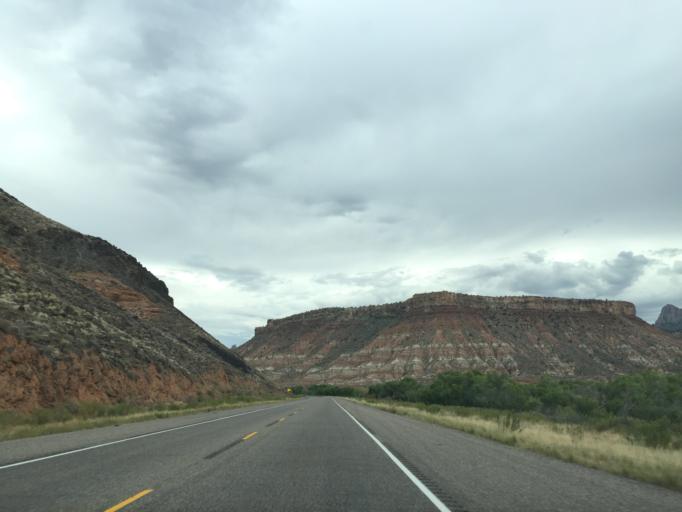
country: US
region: Utah
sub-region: Washington County
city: LaVerkin
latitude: 37.1709
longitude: -113.1076
